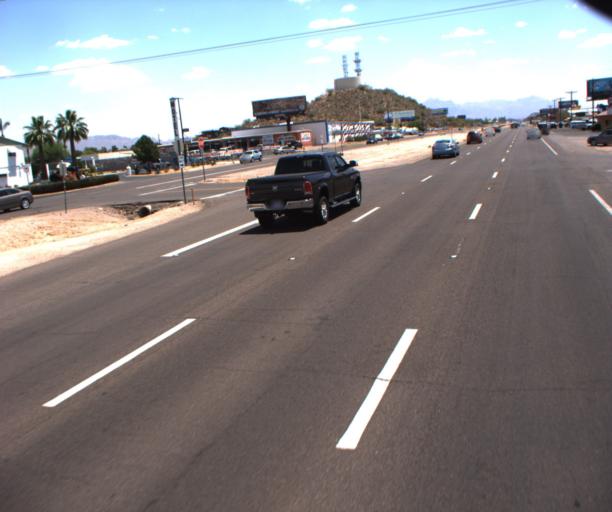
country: US
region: Arizona
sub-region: Pinal County
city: Apache Junction
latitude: 33.4151
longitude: -111.6591
